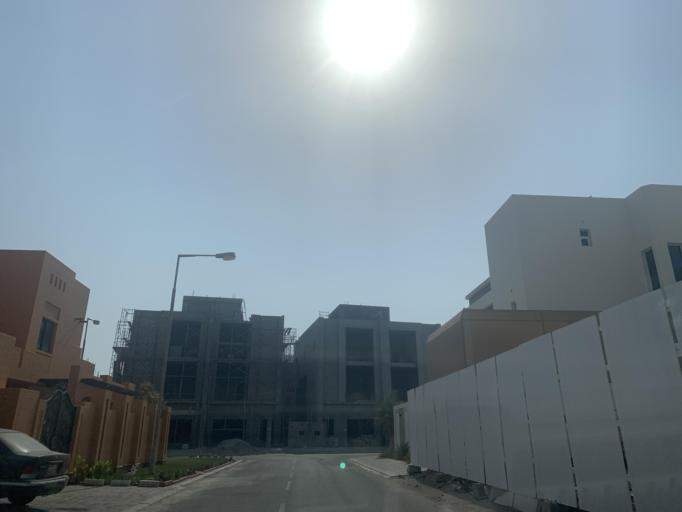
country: BH
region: Manama
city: Jidd Hafs
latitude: 26.2041
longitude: 50.4924
